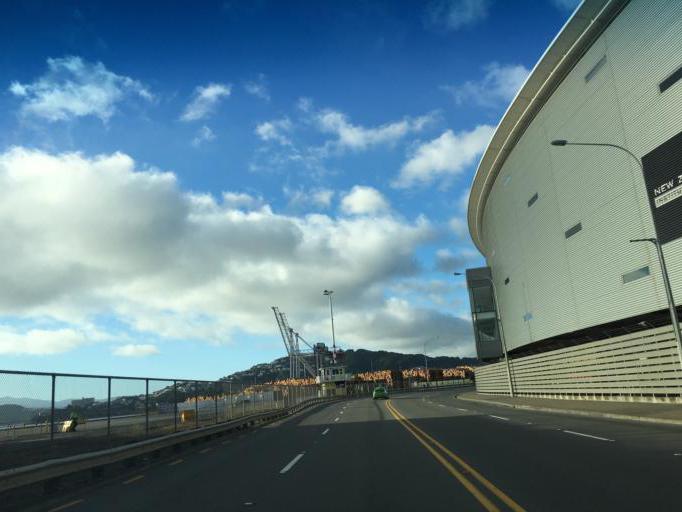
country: NZ
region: Wellington
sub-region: Wellington City
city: Wellington
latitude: -41.2721
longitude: 174.7870
